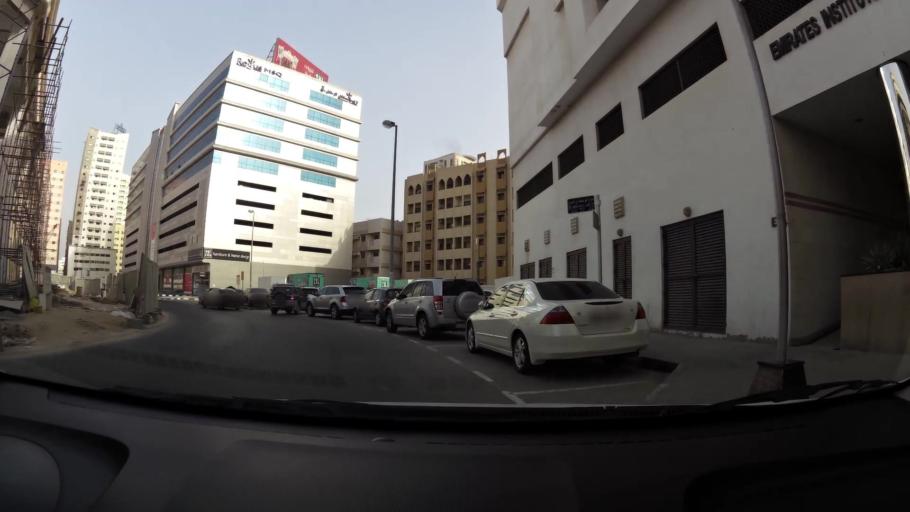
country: AE
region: Ash Shariqah
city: Sharjah
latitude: 25.3438
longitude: 55.3979
